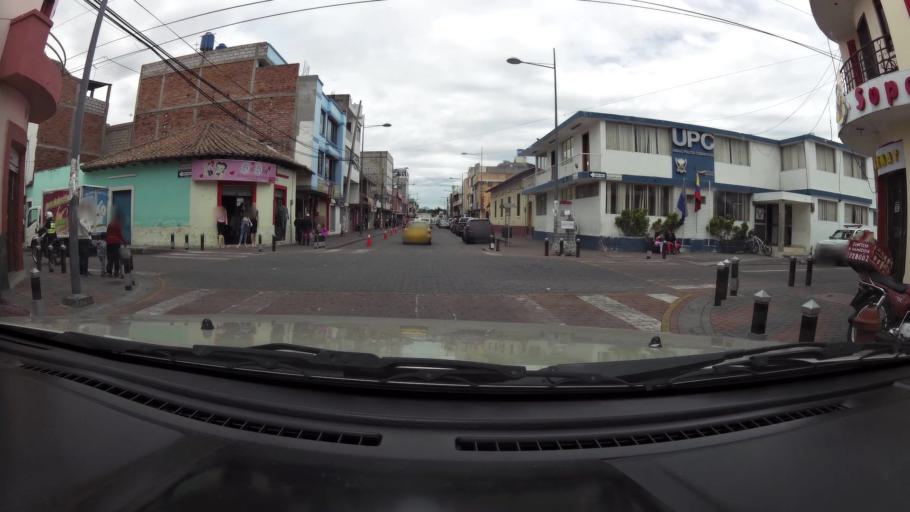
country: EC
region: Cotopaxi
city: San Miguel de Salcedo
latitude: -1.0369
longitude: -78.5891
